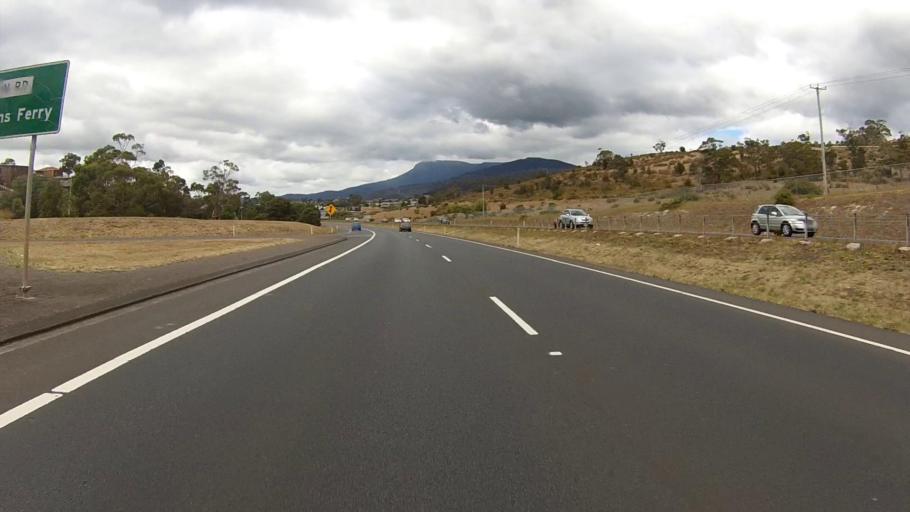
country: AU
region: Tasmania
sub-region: Glenorchy
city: Claremont
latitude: -42.7788
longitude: 147.2384
